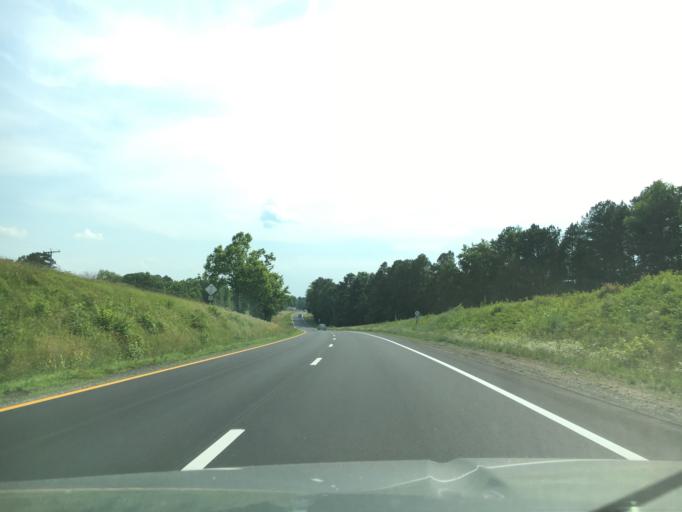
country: US
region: Virginia
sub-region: Halifax County
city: Halifax
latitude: 36.8022
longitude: -78.7725
